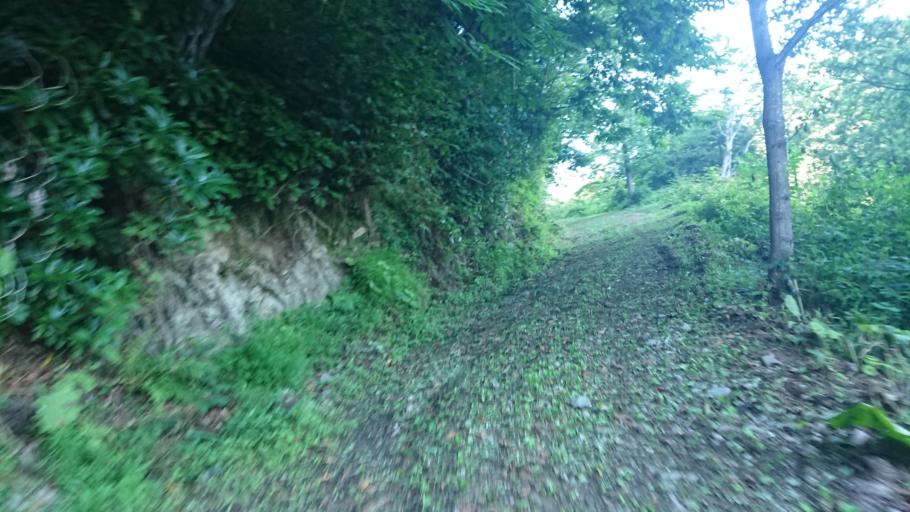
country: TR
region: Rize
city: Rize
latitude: 40.9744
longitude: 40.4976
